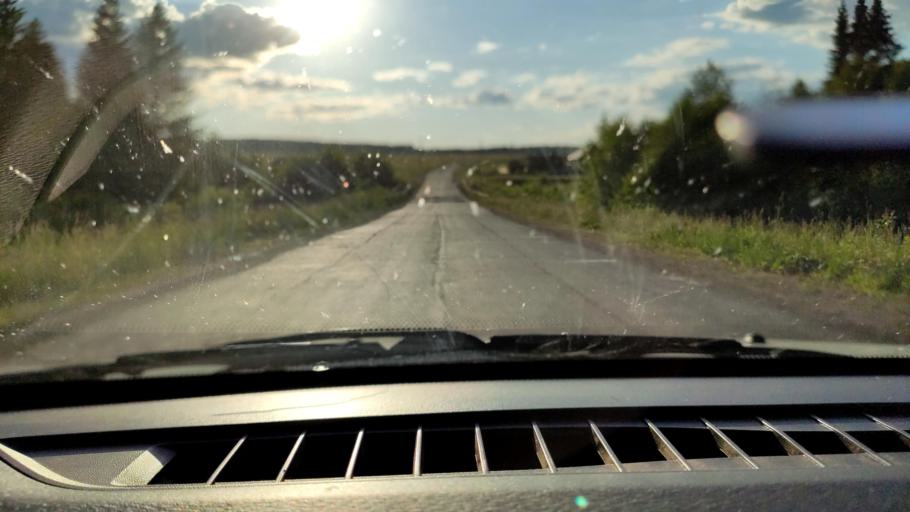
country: RU
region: Perm
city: Uinskoye
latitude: 57.0724
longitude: 56.5646
